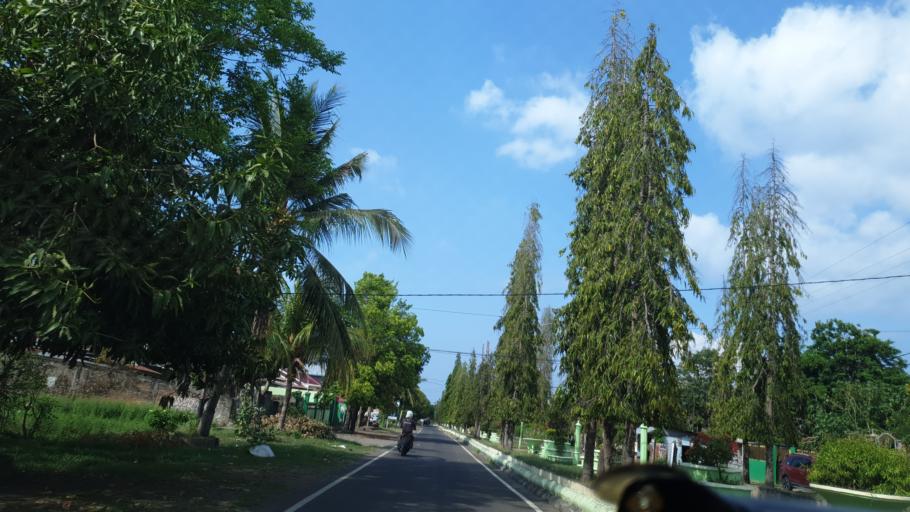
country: ID
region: East Nusa Tenggara
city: Waioti
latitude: -8.6323
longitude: 122.2362
